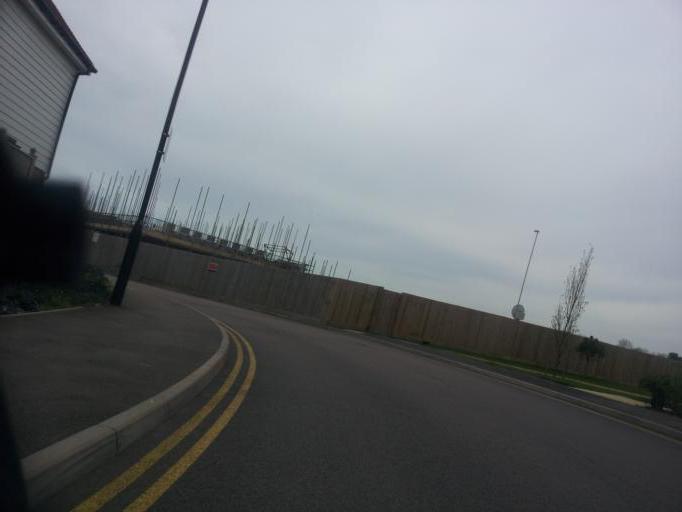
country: GB
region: England
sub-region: Kent
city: Snodland
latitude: 51.3358
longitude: 0.4361
